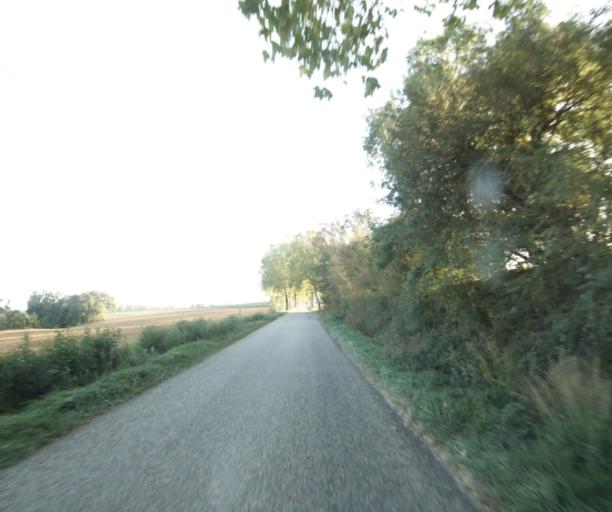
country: FR
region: Midi-Pyrenees
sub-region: Departement du Gers
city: Gondrin
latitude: 43.8824
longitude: 0.2888
